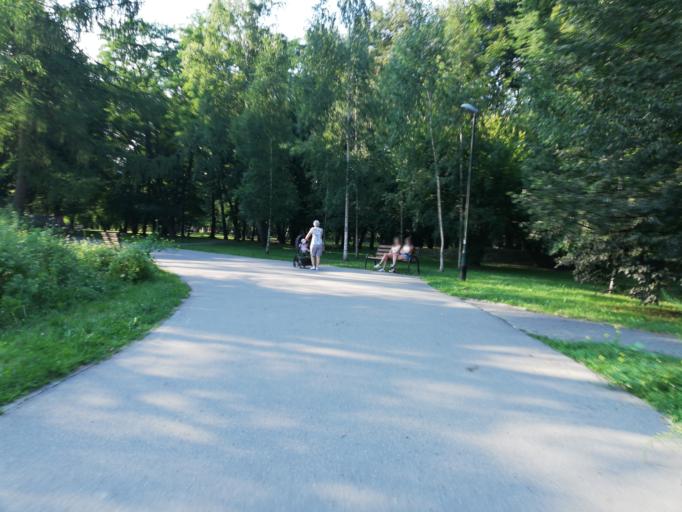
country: PL
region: Lesser Poland Voivodeship
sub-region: Krakow
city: Krakow
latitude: 50.0836
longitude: 20.0080
